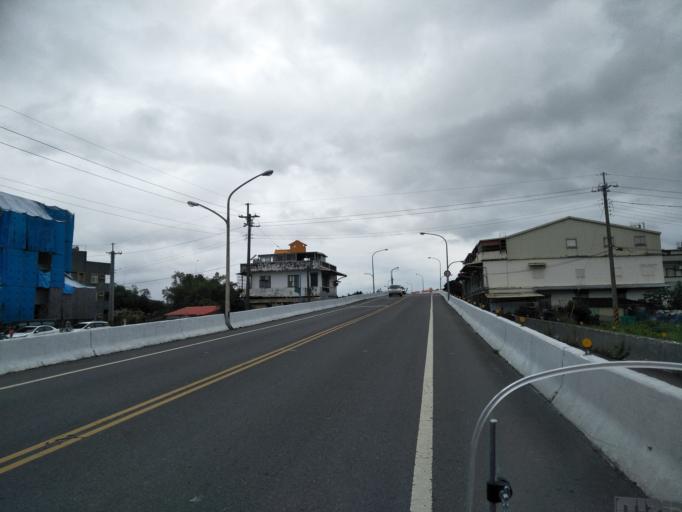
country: TW
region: Taiwan
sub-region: Yilan
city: Yilan
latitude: 24.8105
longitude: 121.7919
